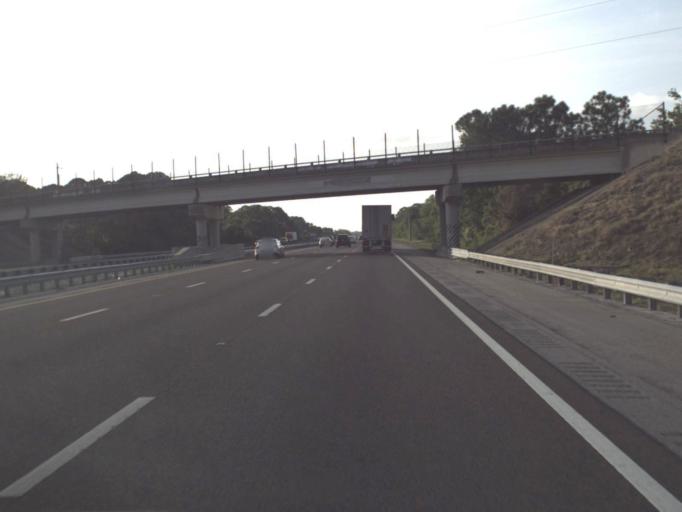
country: US
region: Florida
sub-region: Brevard County
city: Port Saint John
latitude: 28.4859
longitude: -80.8259
